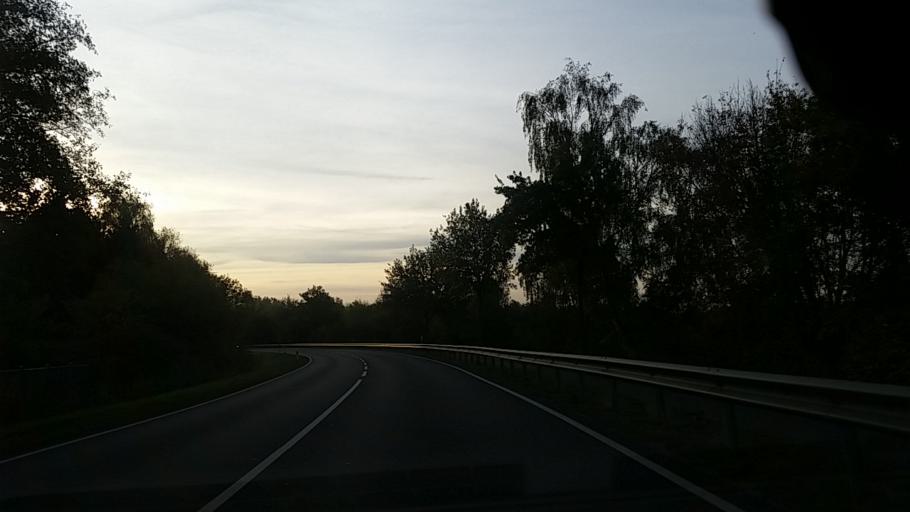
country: DE
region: Lower Saxony
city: Wolfsburg
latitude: 52.4373
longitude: 10.8305
